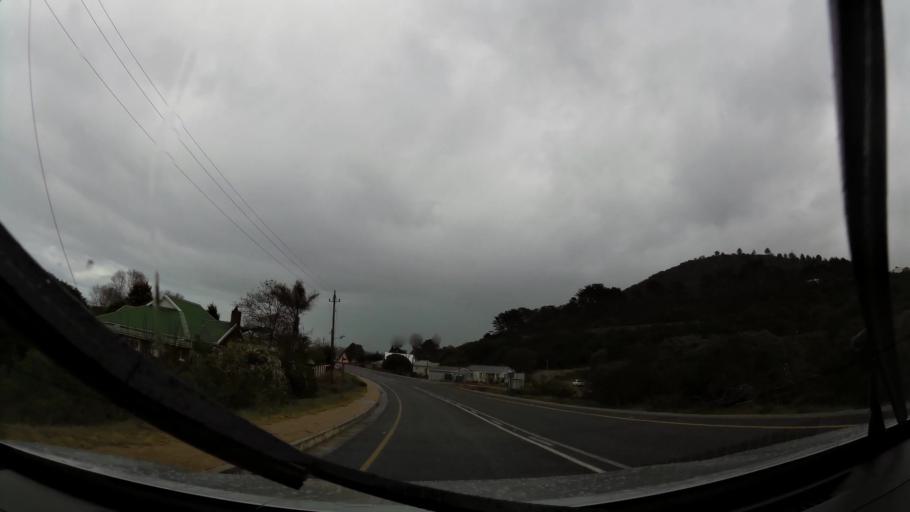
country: ZA
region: Western Cape
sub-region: Eden District Municipality
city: Mossel Bay
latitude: -34.0494
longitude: 22.2393
